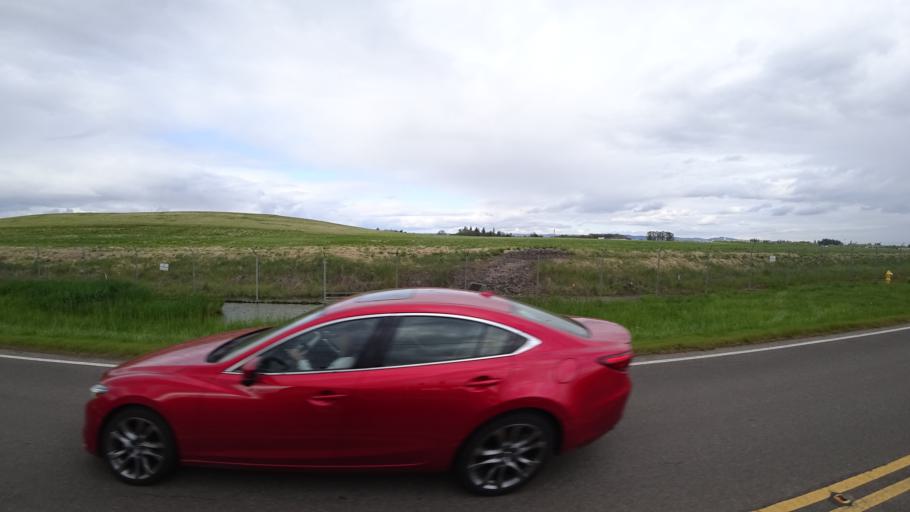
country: US
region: Oregon
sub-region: Washington County
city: Hillsboro
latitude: 45.5474
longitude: -122.9613
